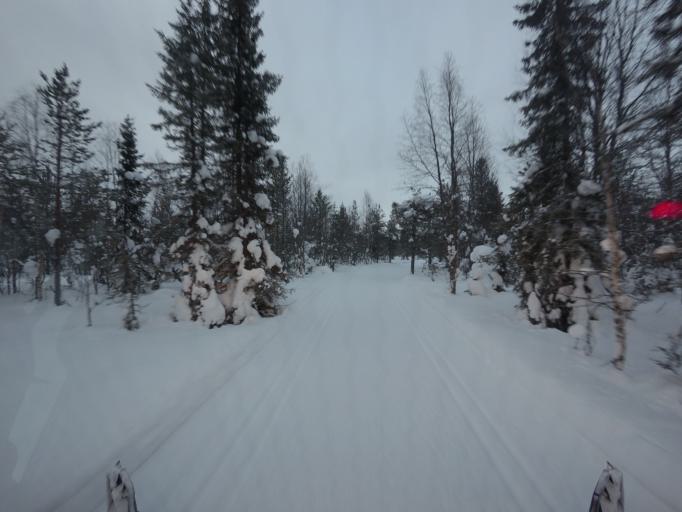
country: FI
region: Lapland
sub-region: Tunturi-Lappi
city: Kolari
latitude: 67.6214
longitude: 24.1411
